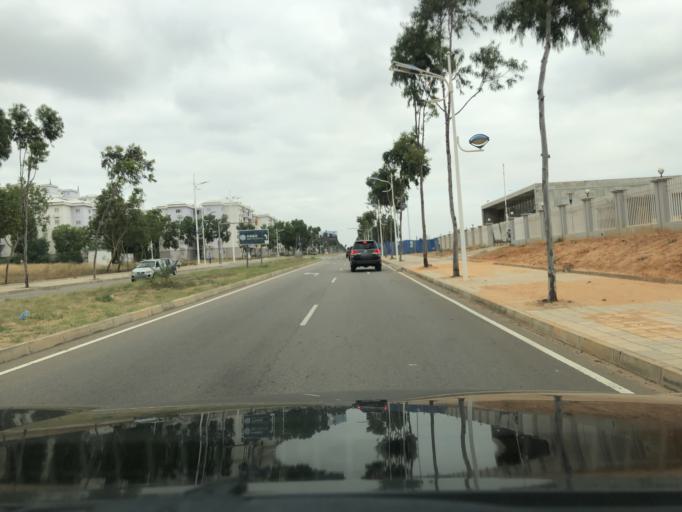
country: AO
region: Luanda
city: Luanda
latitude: -8.9911
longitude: 13.2818
